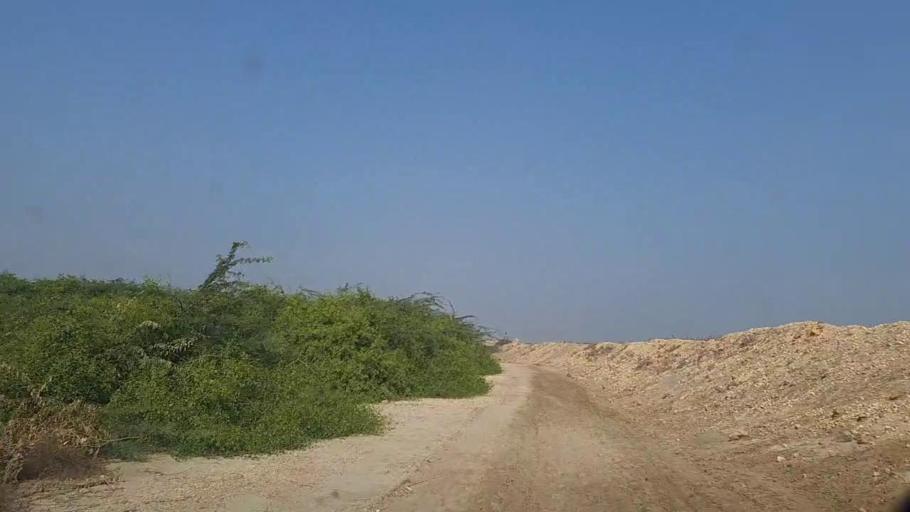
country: PK
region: Sindh
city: Thatta
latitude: 24.6586
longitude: 67.9270
